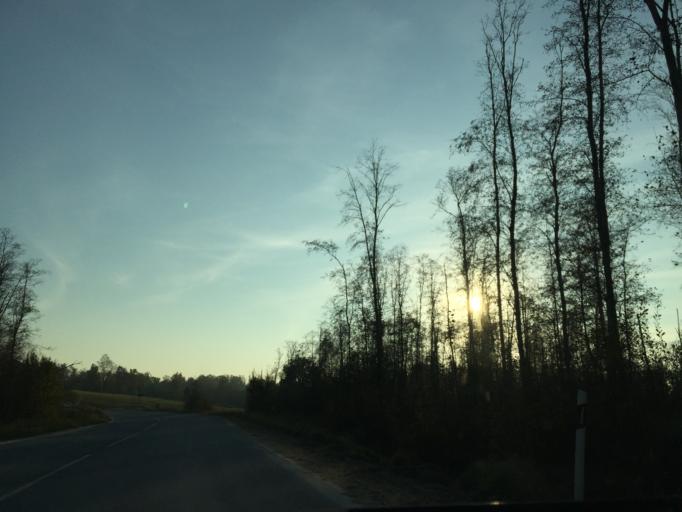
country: LV
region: Vainode
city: Vainode
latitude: 56.5579
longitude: 21.8418
